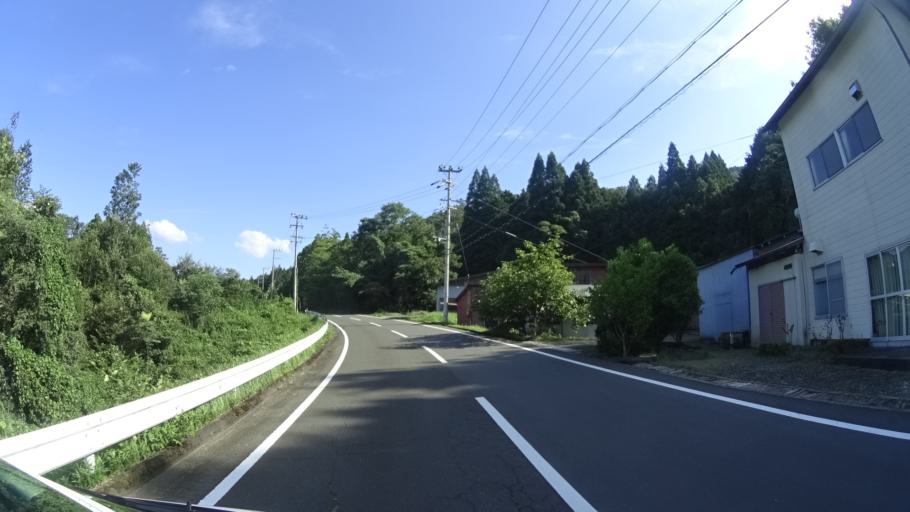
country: JP
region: Kyoto
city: Ayabe
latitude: 35.2903
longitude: 135.3279
